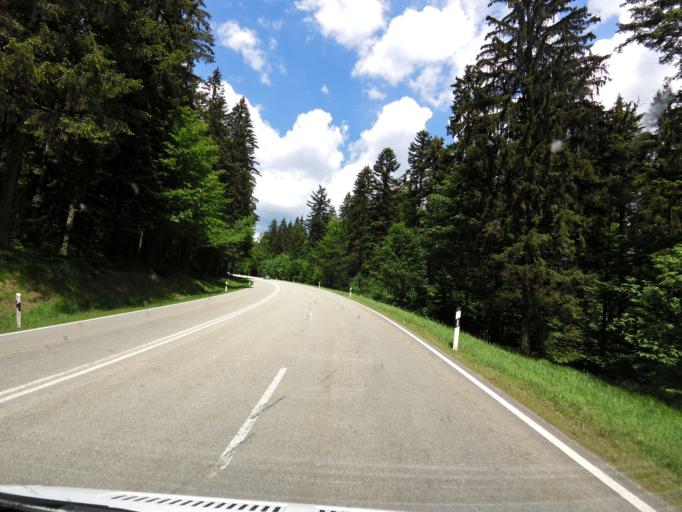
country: DE
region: Bavaria
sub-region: Lower Bavaria
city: Philippsreut
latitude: 48.8482
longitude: 13.6725
